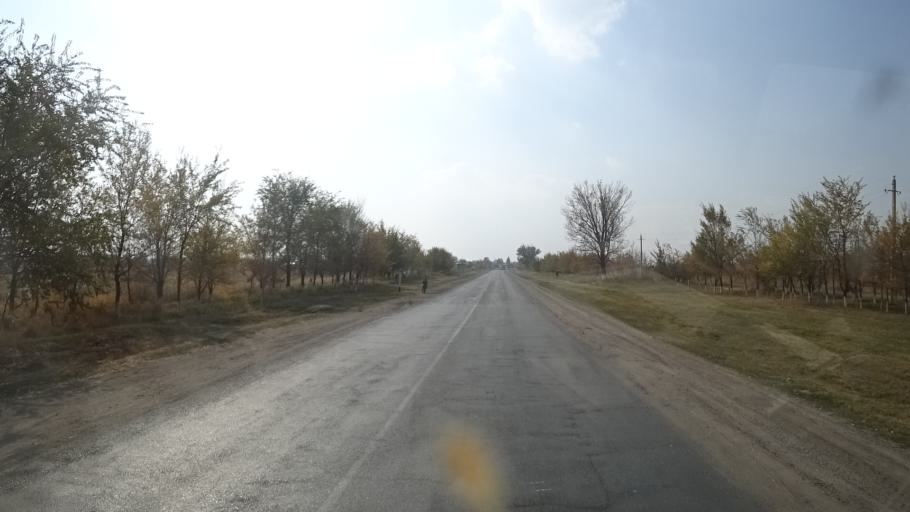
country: KZ
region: Zhambyl
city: Taraz
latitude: 42.9369
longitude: 71.4431
